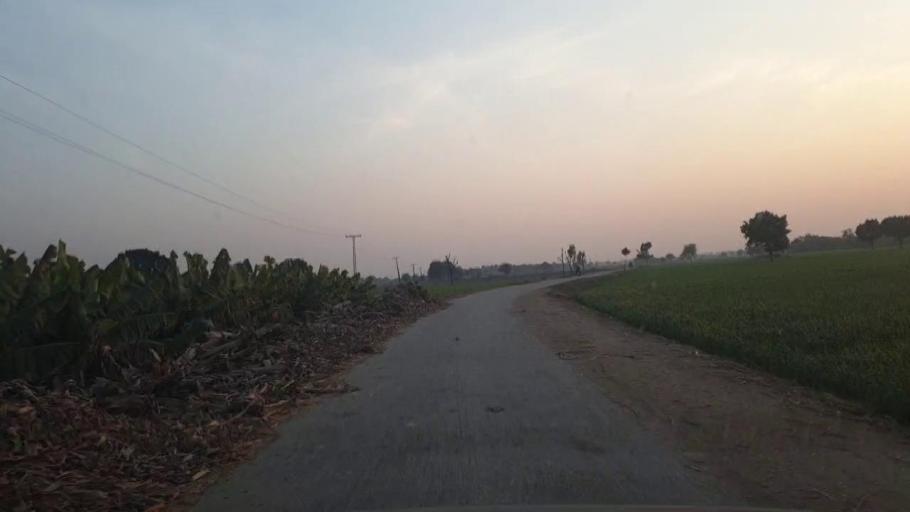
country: PK
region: Sindh
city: Bhit Shah
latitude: 25.8596
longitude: 68.5151
